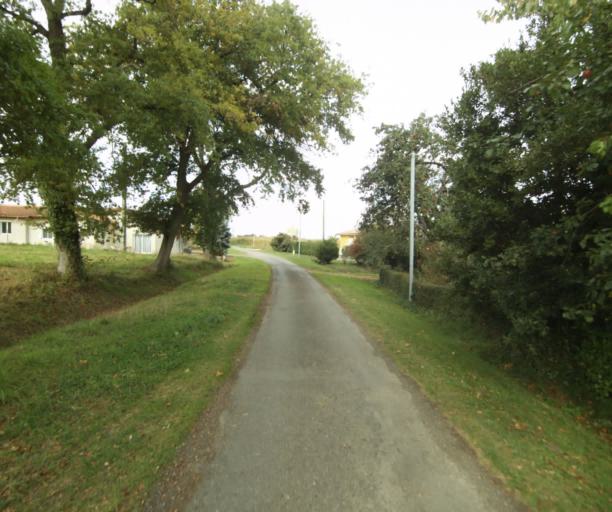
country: FR
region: Midi-Pyrenees
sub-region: Departement du Gers
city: Eauze
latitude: 43.8375
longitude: 0.0973
